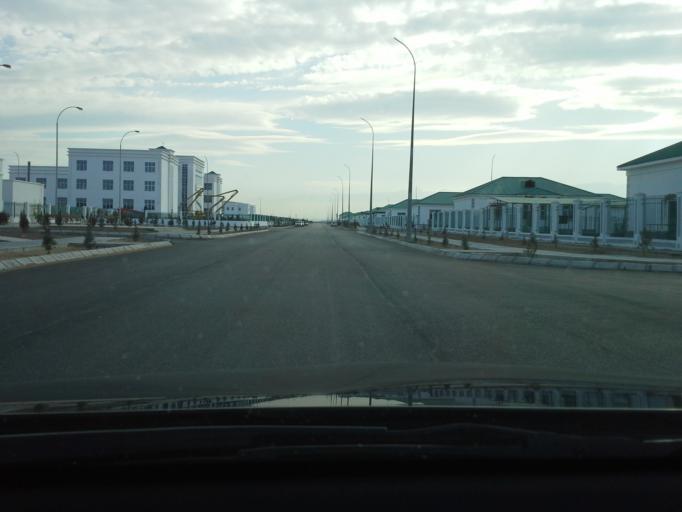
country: TM
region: Ahal
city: Abadan
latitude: 38.0995
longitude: 58.3084
